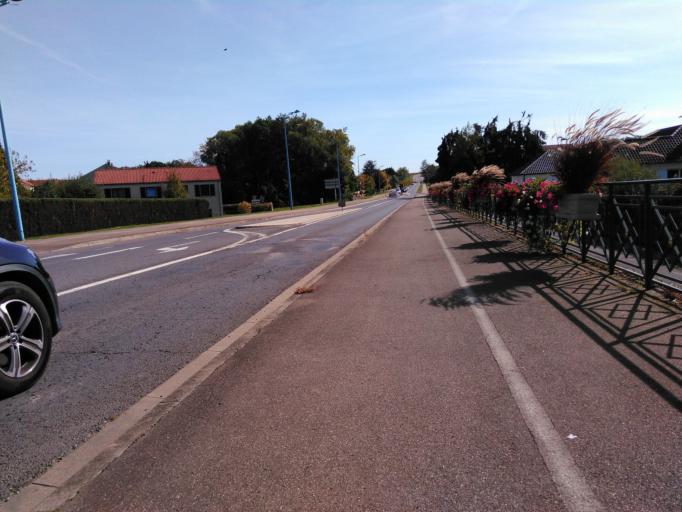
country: FR
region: Lorraine
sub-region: Departement de la Moselle
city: Hettange-Grande
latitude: 49.3973
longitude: 6.1630
